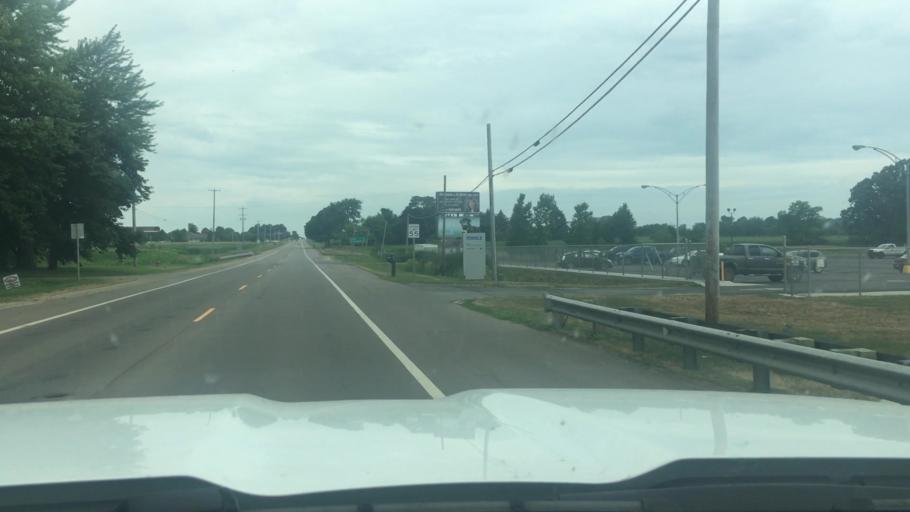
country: US
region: Michigan
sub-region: Clinton County
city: Saint Johns
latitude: 43.0016
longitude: -84.5725
